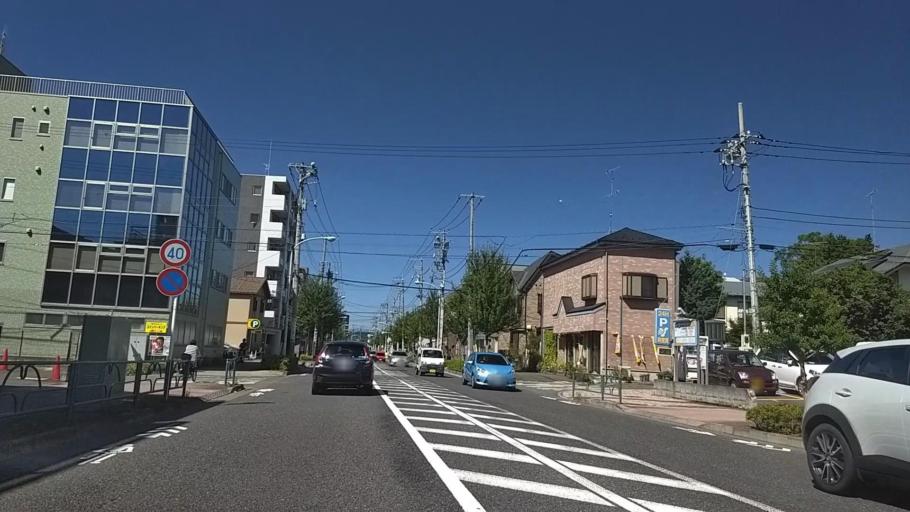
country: JP
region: Tokyo
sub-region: Machida-shi
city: Machida
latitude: 35.5833
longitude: 139.4775
